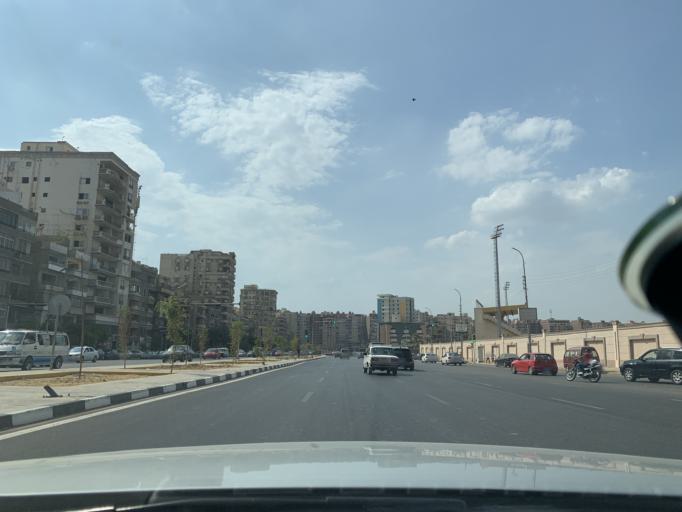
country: EG
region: Muhafazat al Qalyubiyah
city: Al Khankah
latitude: 30.1148
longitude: 31.3434
